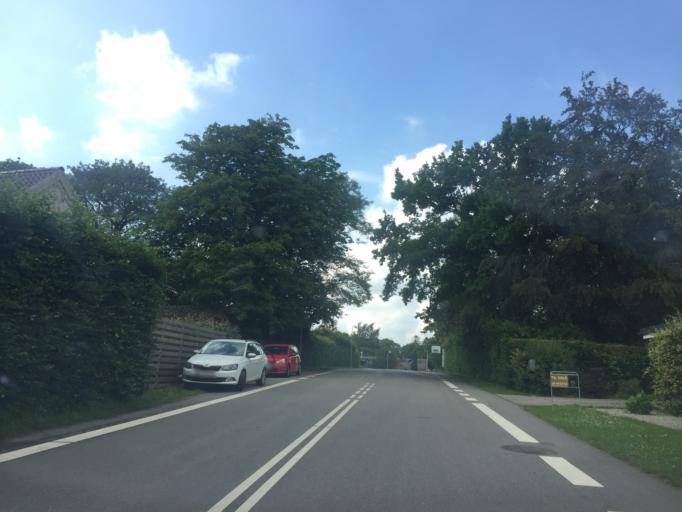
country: DK
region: Zealand
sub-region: Roskilde Kommune
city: Gundsomagle
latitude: 55.7067
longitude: 12.1624
